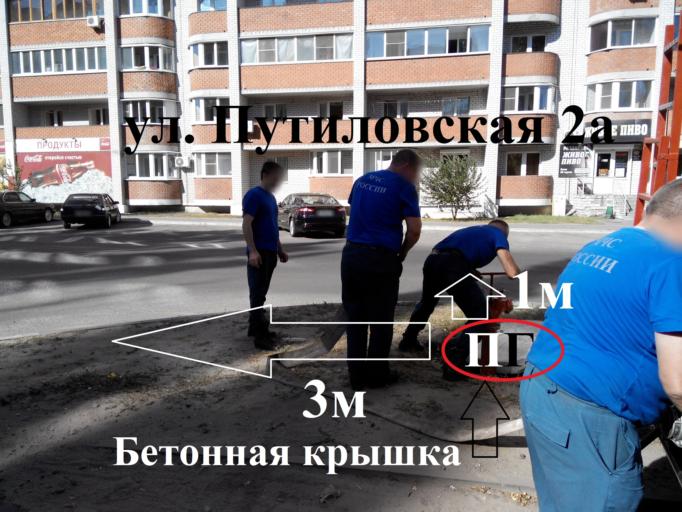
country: RU
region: Voronezj
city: Voronezh
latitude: 51.6580
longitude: 39.1297
